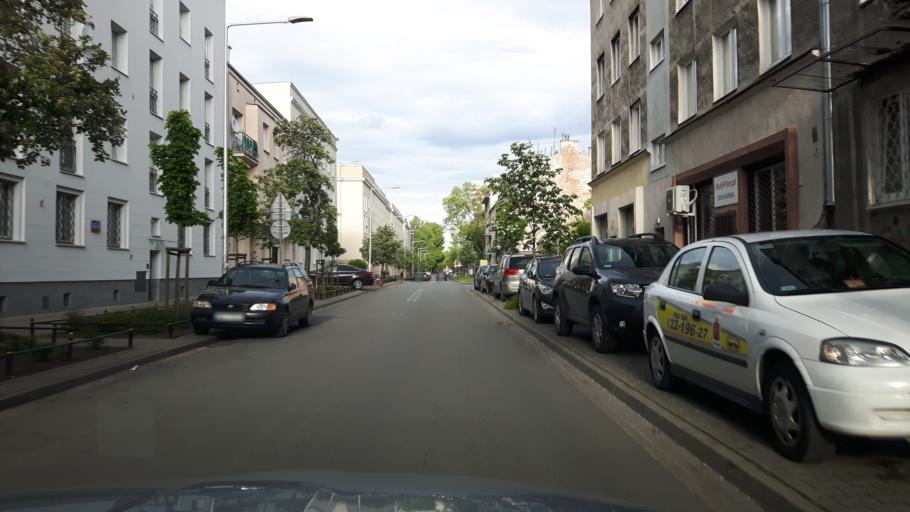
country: PL
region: Masovian Voivodeship
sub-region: Warszawa
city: Praga Poludnie
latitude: 52.2475
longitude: 21.0806
